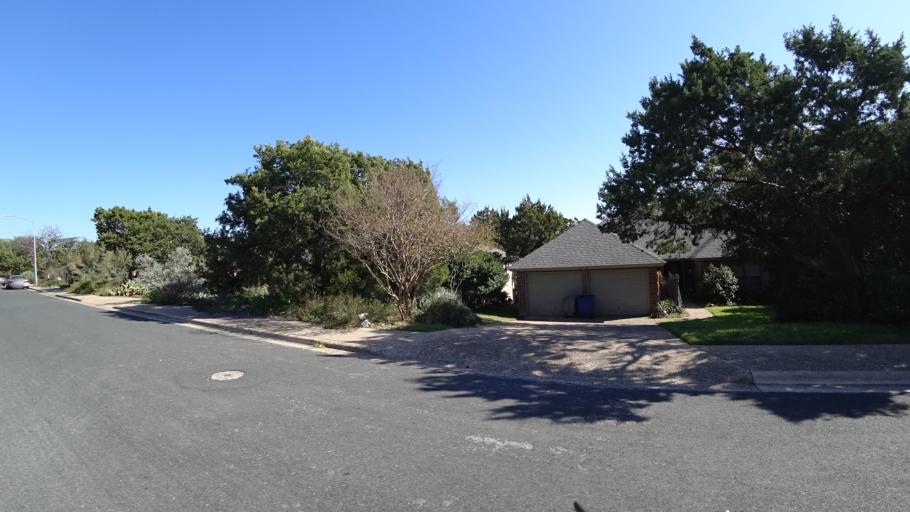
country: US
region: Texas
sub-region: Williamson County
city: Jollyville
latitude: 30.4135
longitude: -97.7581
